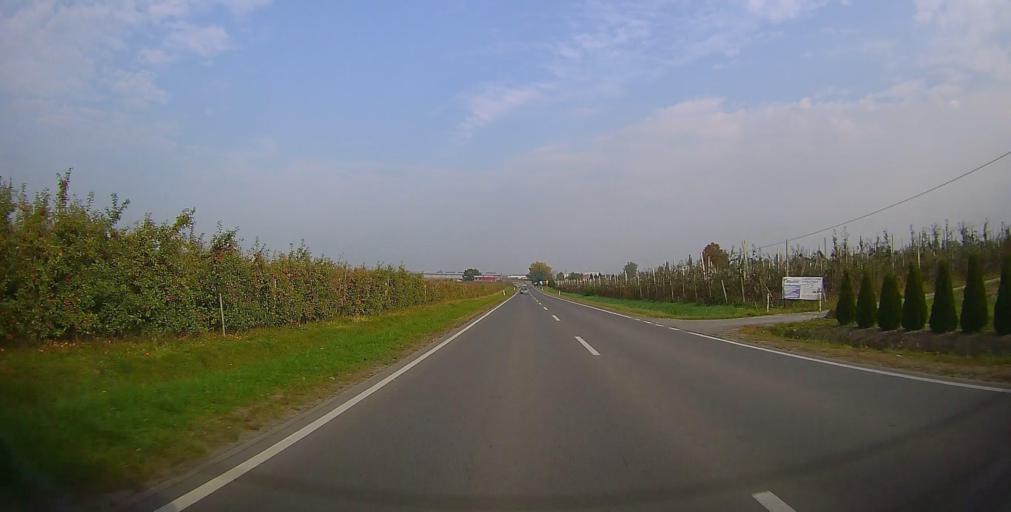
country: PL
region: Masovian Voivodeship
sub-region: Powiat grojecki
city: Mogielnica
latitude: 51.7179
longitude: 20.7456
